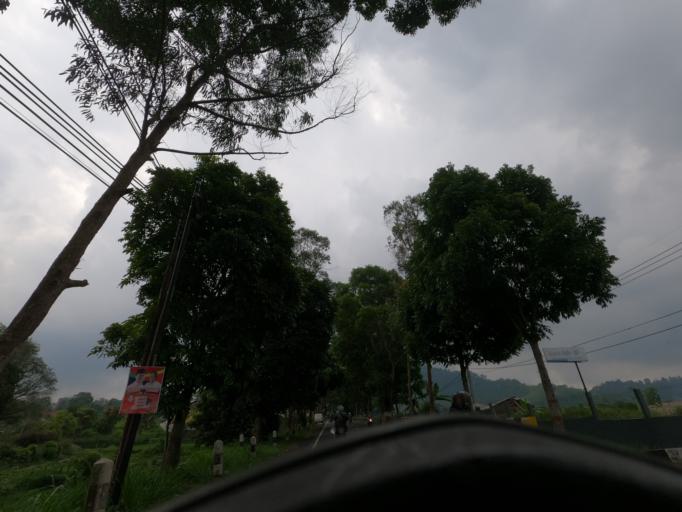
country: ID
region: West Java
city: Sukabumi
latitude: -6.7742
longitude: 107.0635
